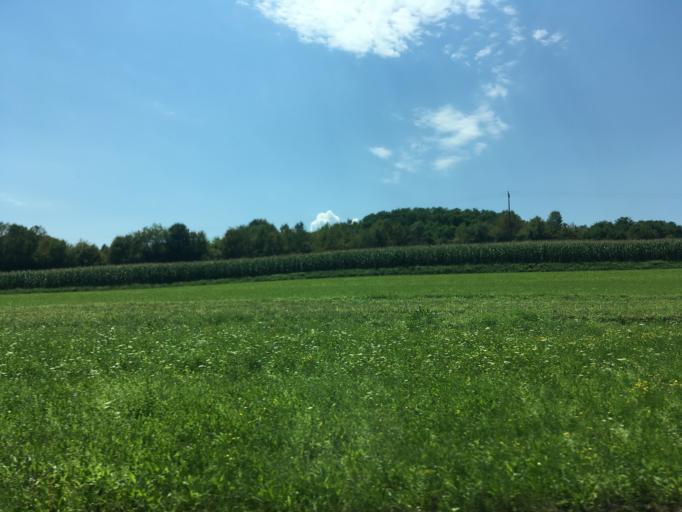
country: SI
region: Metlika
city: Metlika
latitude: 45.6018
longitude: 15.3356
